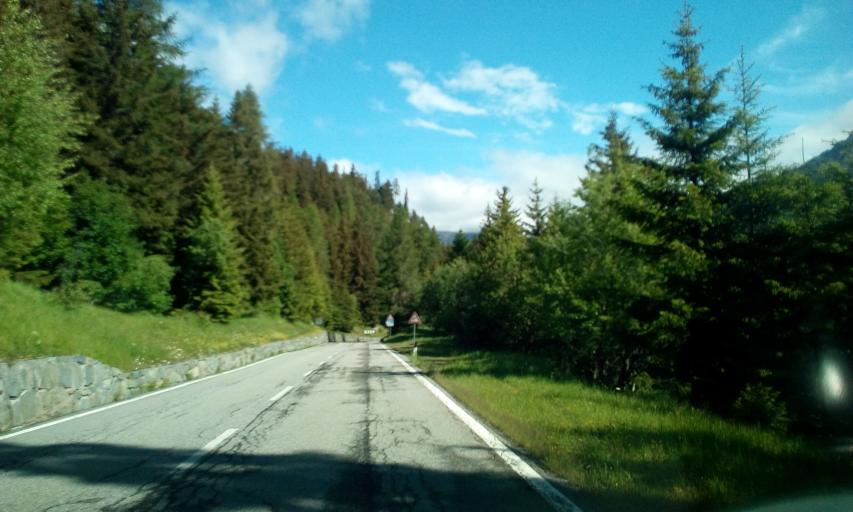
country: IT
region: Aosta Valley
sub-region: Valle d'Aosta
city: Brusson
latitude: 45.7578
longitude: 7.7090
